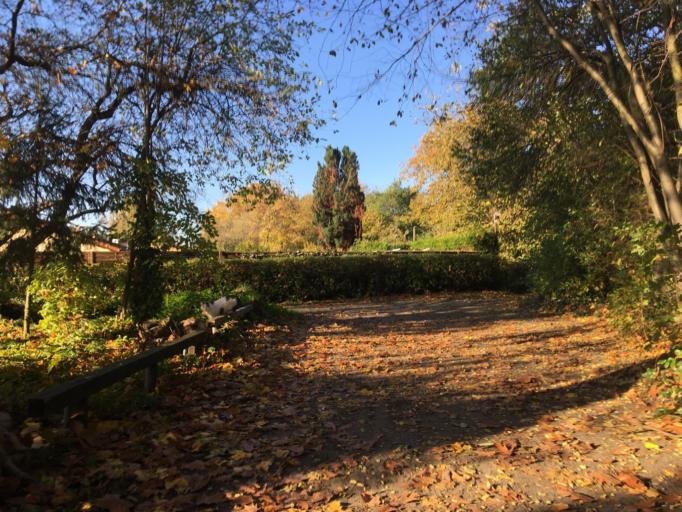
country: DE
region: Berlin
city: Markisches Viertel
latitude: 52.5888
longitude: 13.3486
